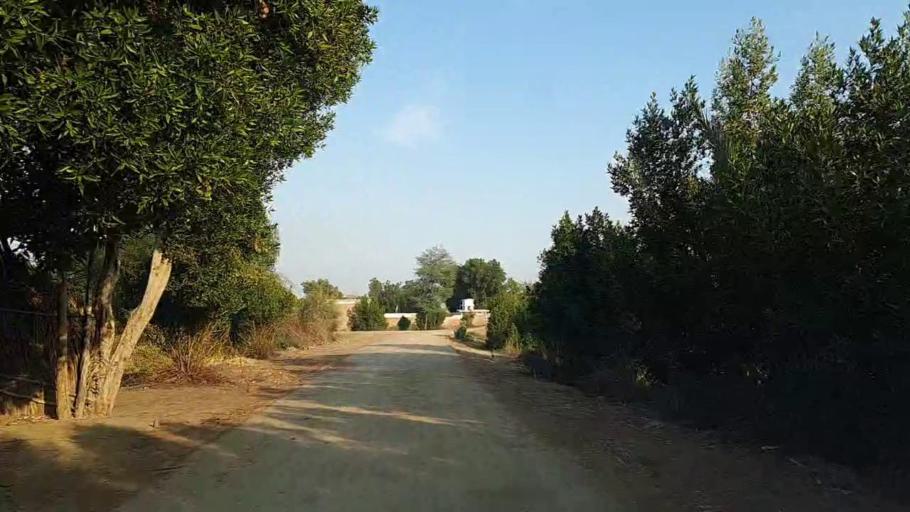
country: PK
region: Sindh
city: Jam Sahib
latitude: 26.3816
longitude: 68.5294
